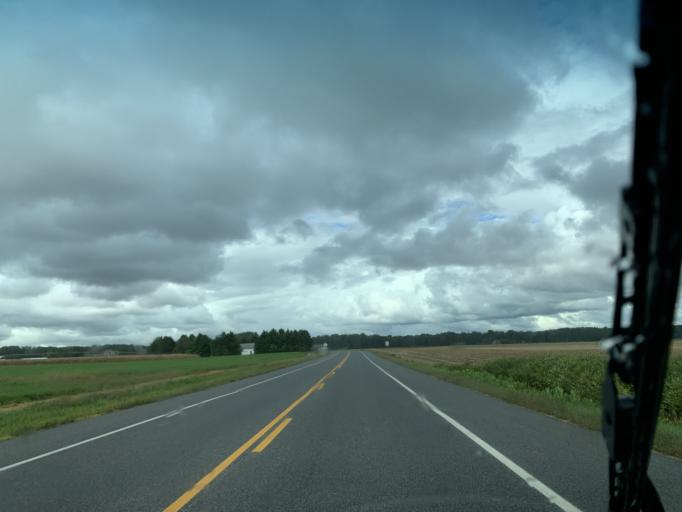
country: US
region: Maryland
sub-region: Caroline County
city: Ridgely
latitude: 39.0016
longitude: -75.8739
